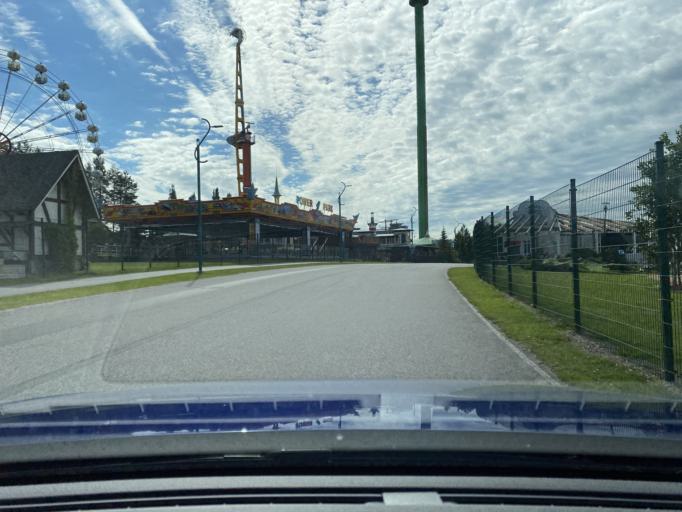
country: FI
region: Southern Ostrobothnia
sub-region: Seinaejoki
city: Alahaermae
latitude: 63.2293
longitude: 22.8575
